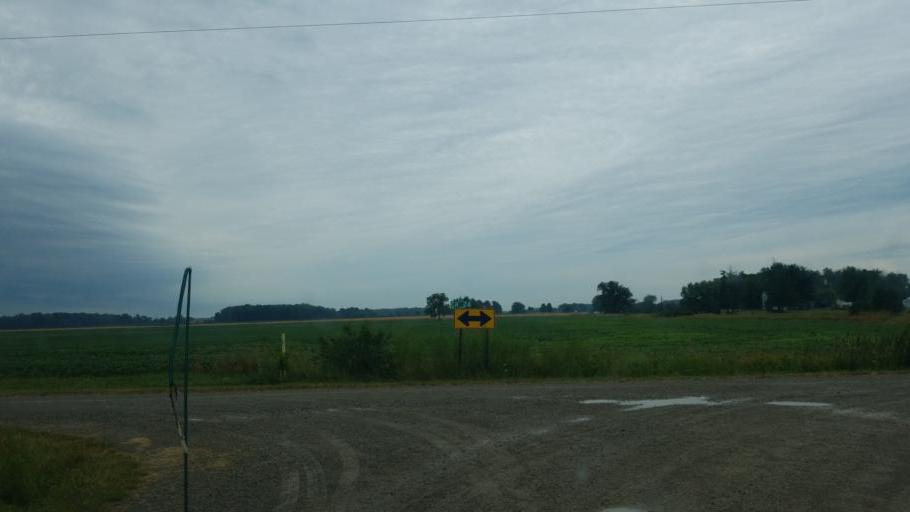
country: US
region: Indiana
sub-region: DeKalb County
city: Butler
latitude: 41.4429
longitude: -84.9097
